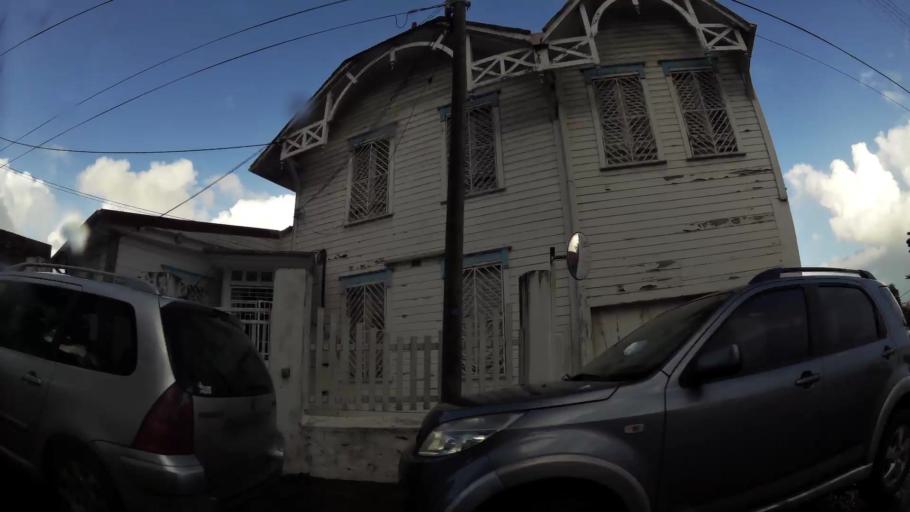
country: MQ
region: Martinique
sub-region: Martinique
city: Fort-de-France
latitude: 14.6089
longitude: -61.0756
